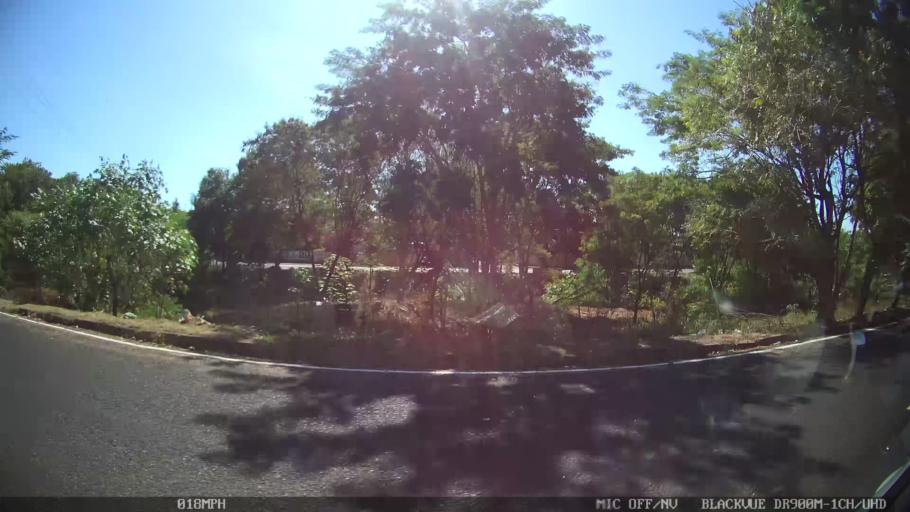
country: BR
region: Sao Paulo
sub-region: Sao Jose Do Rio Preto
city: Sao Jose do Rio Preto
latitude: -20.7733
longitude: -49.4033
